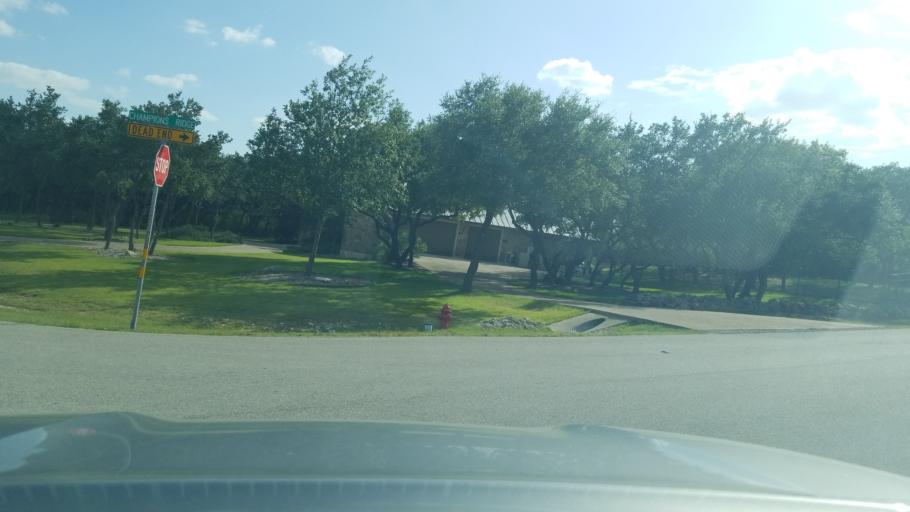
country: US
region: Texas
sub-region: Comal County
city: Bulverde
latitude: 29.8105
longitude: -98.3977
